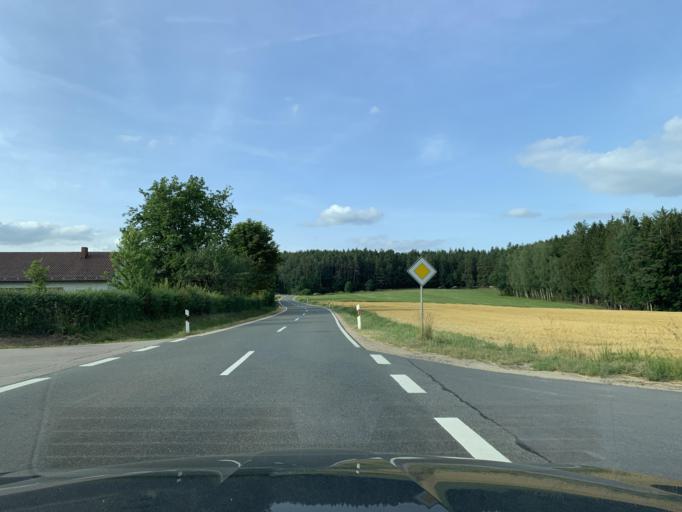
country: DE
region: Bavaria
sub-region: Upper Palatinate
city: Schwarzhofen
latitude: 49.3960
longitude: 12.3574
